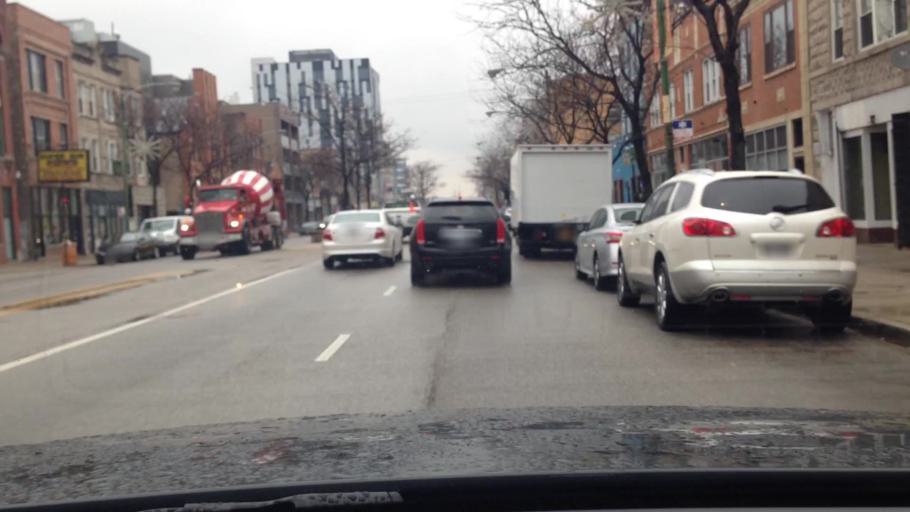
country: US
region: Illinois
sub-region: Cook County
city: Chicago
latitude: 41.9007
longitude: -87.6674
